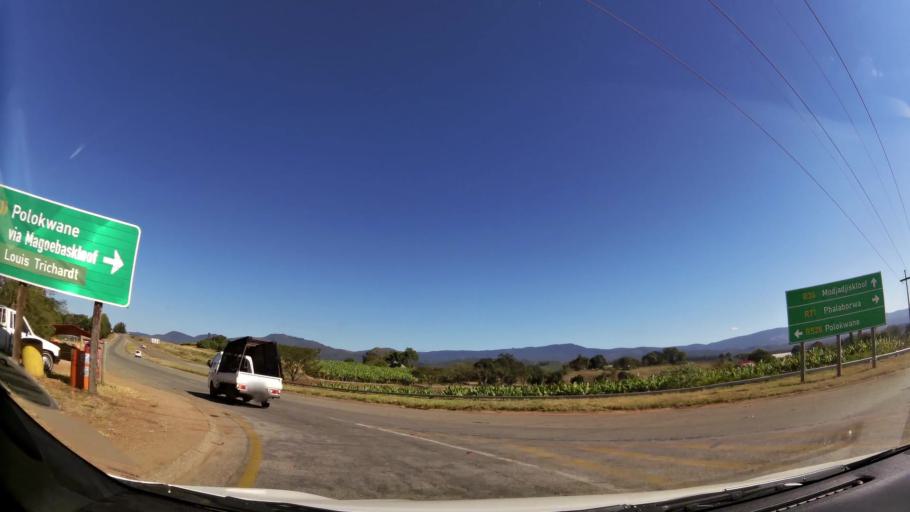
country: ZA
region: Limpopo
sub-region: Mopani District Municipality
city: Tzaneen
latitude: -23.8365
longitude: 30.1357
